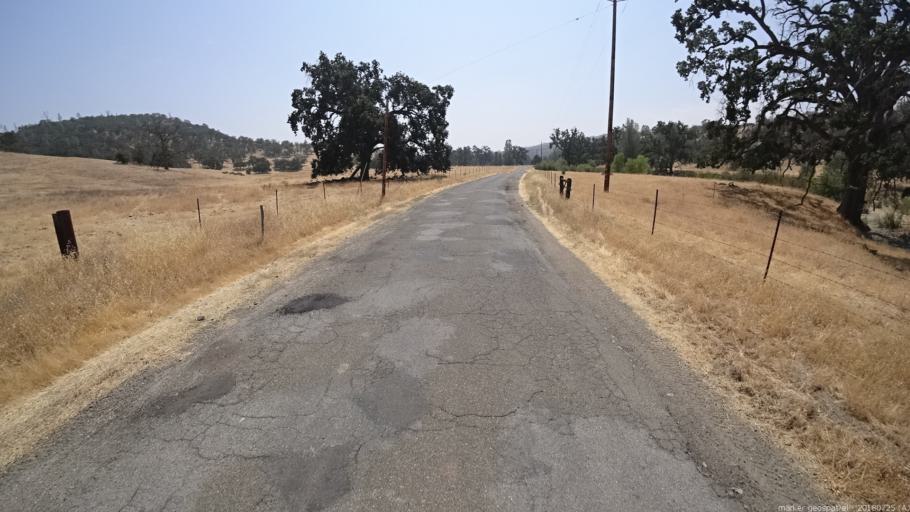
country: US
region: California
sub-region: Fresno County
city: Coalinga
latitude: 35.9404
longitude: -120.4625
